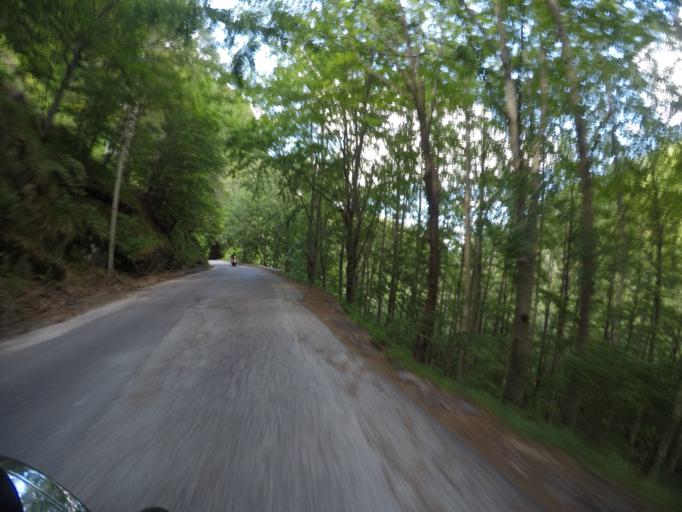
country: IT
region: Tuscany
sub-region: Provincia di Lucca
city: Minucciano
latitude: 44.1432
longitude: 10.1934
